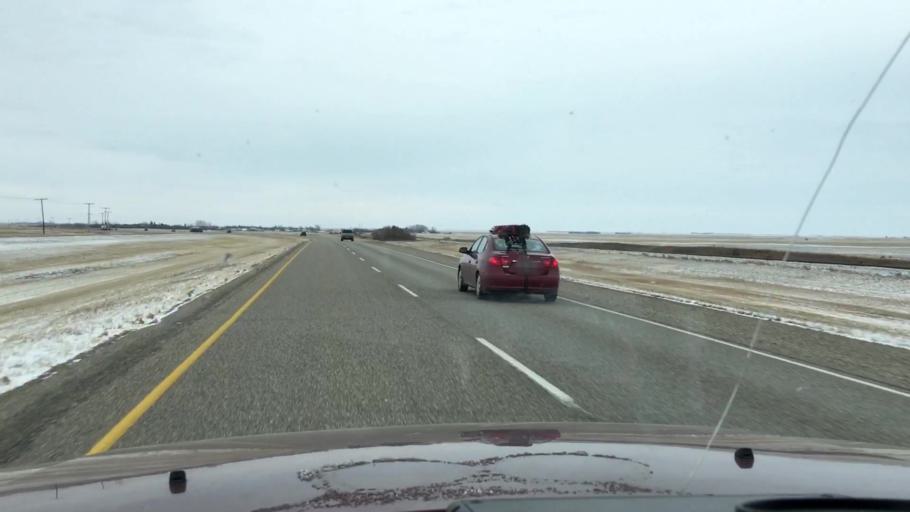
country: CA
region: Saskatchewan
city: Watrous
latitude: 51.1742
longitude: -105.9336
